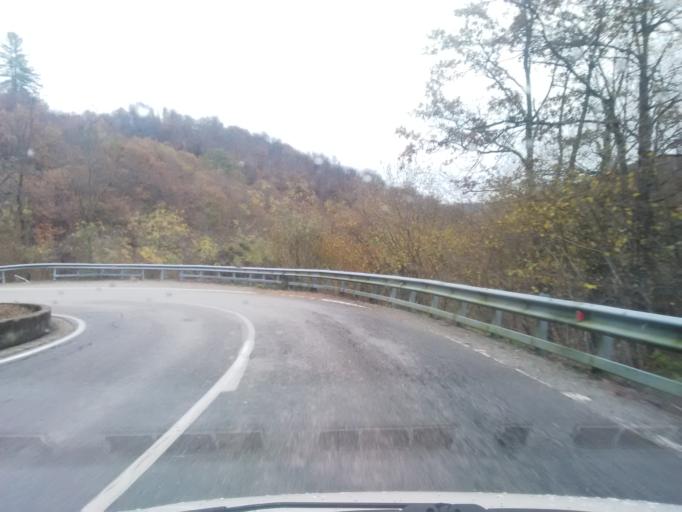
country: IT
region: Piedmont
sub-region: Provincia di Novara
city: Pogno
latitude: 45.7442
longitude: 8.3718
